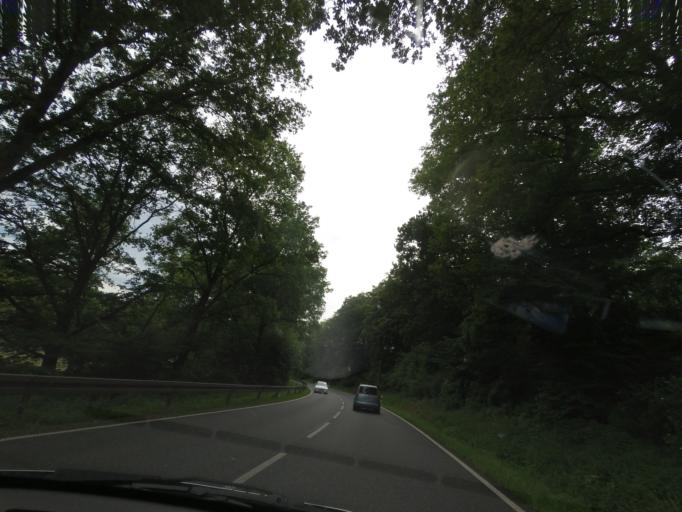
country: DE
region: Hesse
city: Stadtallendorf
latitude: 50.7830
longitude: 9.0375
